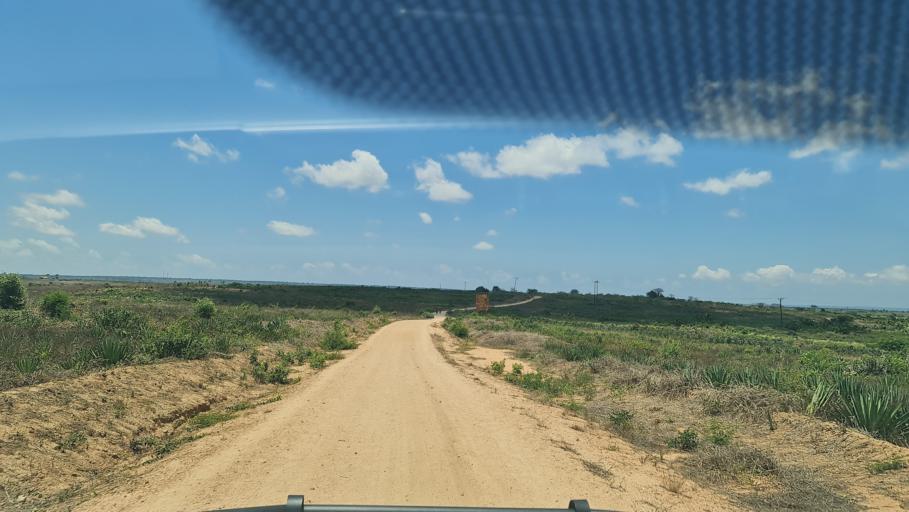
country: MZ
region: Nampula
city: Nacala
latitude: -14.3295
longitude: 40.5965
